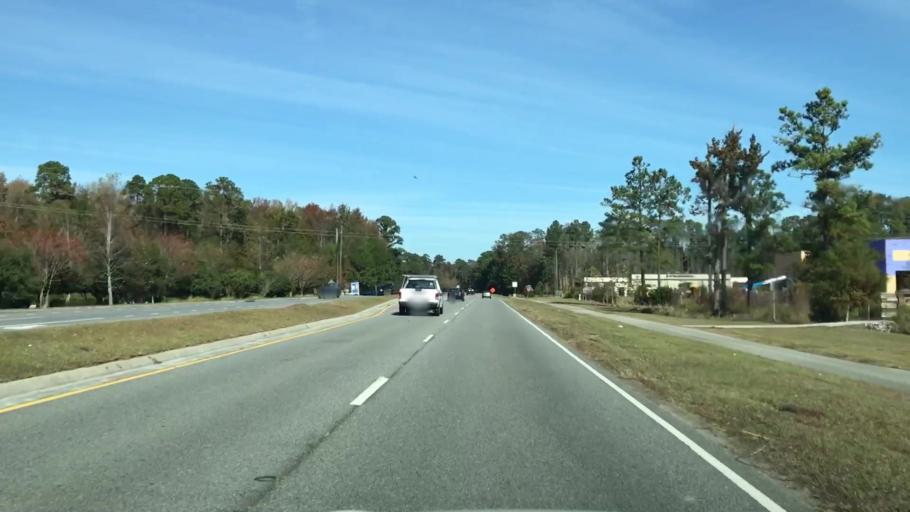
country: US
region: South Carolina
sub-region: Beaufort County
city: Bluffton
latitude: 32.2837
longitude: -80.9104
